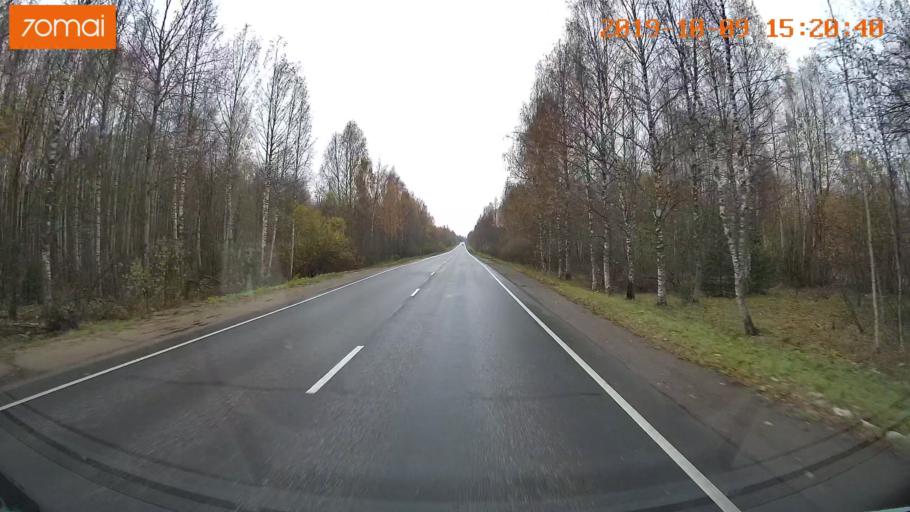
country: RU
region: Kostroma
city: Susanino
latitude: 58.0620
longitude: 41.5338
